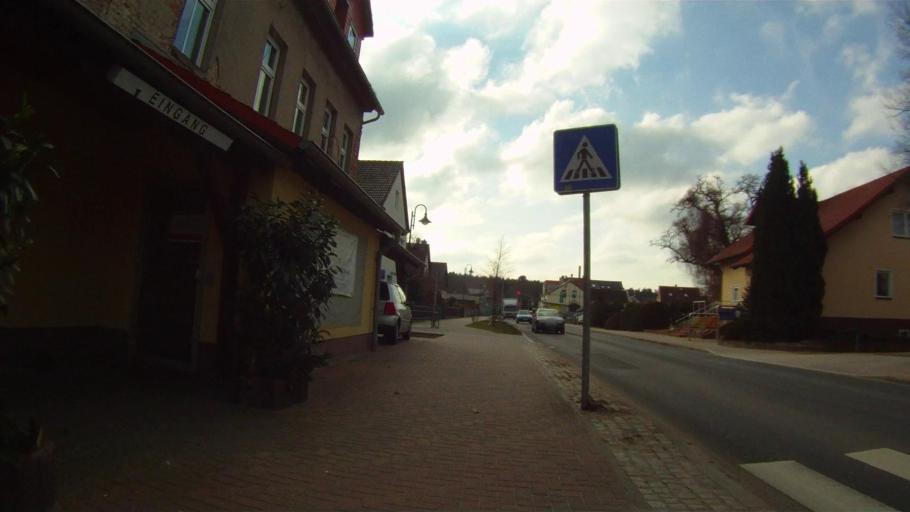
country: DE
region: Brandenburg
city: Erkner
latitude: 52.3900
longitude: 13.7427
